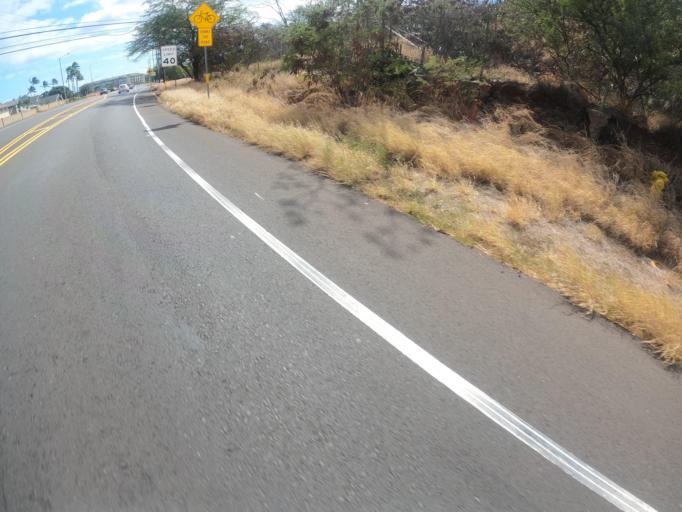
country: US
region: Hawaii
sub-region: Honolulu County
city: Makakilo City
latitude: 21.3355
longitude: -158.0726
